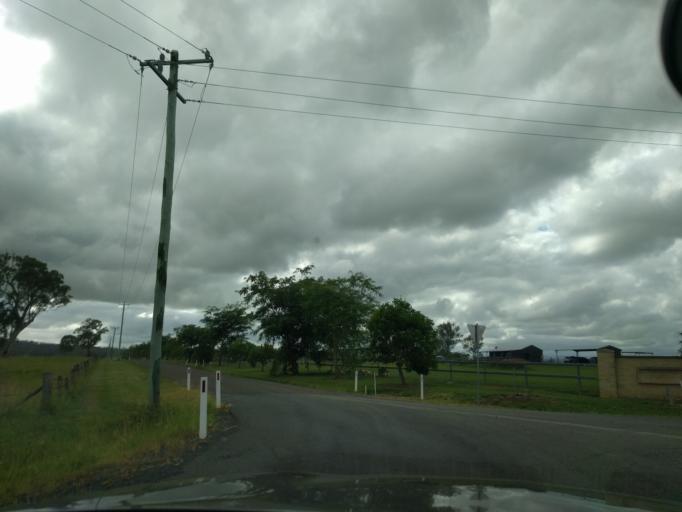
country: AU
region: Queensland
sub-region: Logan
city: Cedar Vale
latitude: -28.0079
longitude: 152.9930
